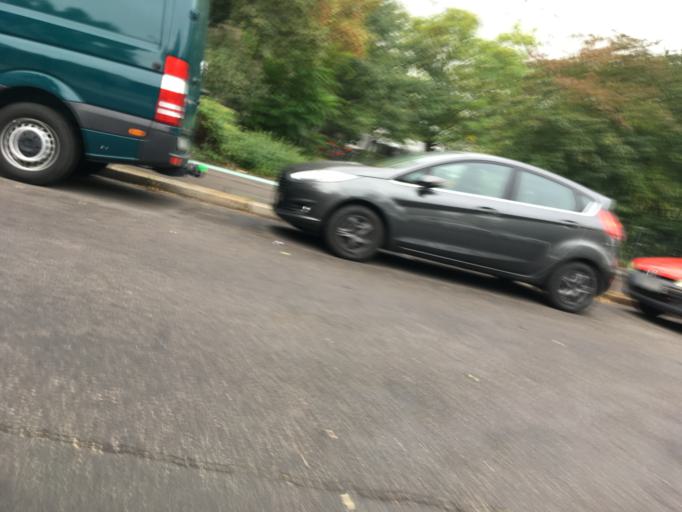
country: DE
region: Berlin
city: Prenzlauer Berg Bezirk
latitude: 52.5250
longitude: 13.4244
